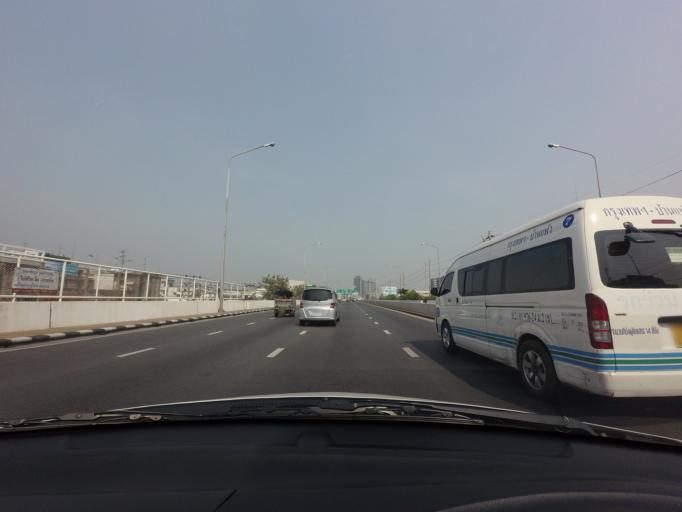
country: TH
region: Bangkok
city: Bangkok Yai
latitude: 13.7204
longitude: 100.4772
